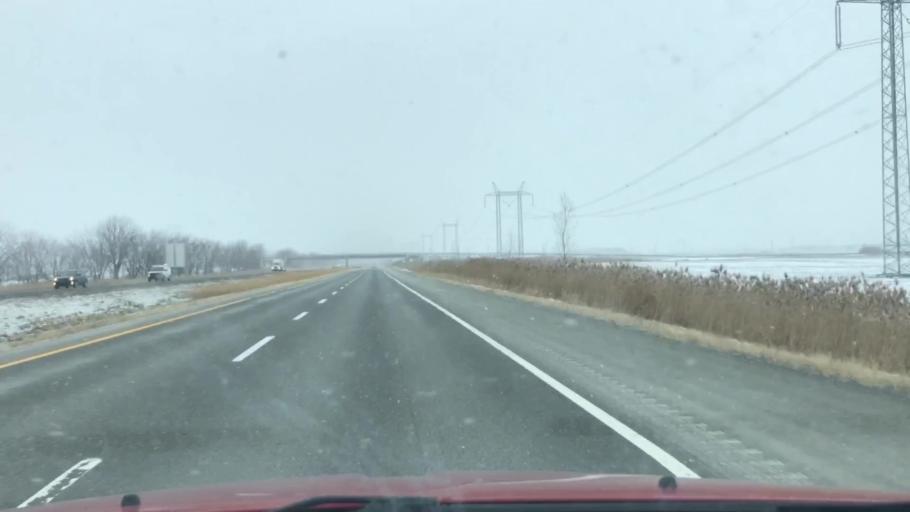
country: CA
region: Quebec
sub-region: Monteregie
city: Rougemont
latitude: 45.3781
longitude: -73.0517
